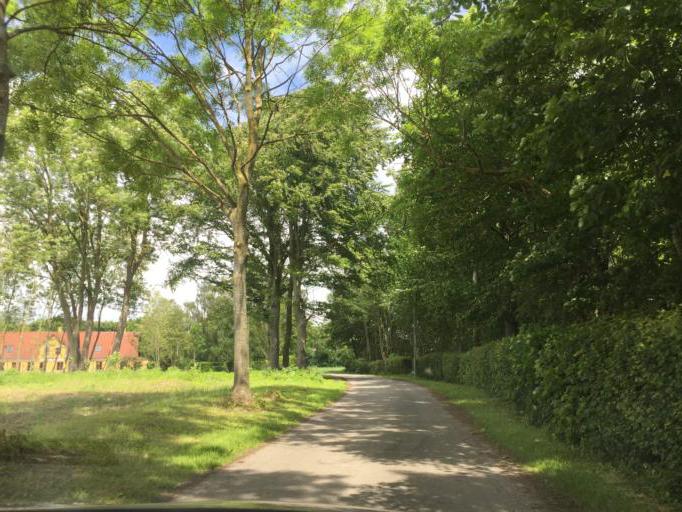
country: DK
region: South Denmark
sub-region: Faaborg-Midtfyn Kommune
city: Ringe
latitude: 55.1991
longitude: 10.4463
